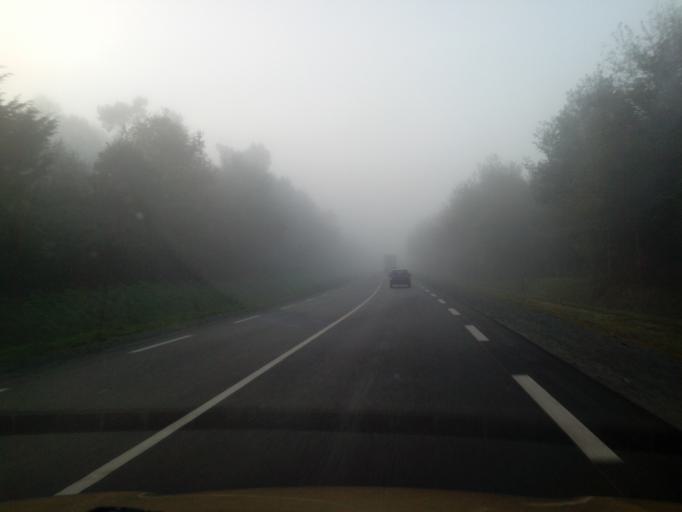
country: FR
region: Brittany
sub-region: Departement du Morbihan
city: Mauron
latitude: 48.0493
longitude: -2.3016
